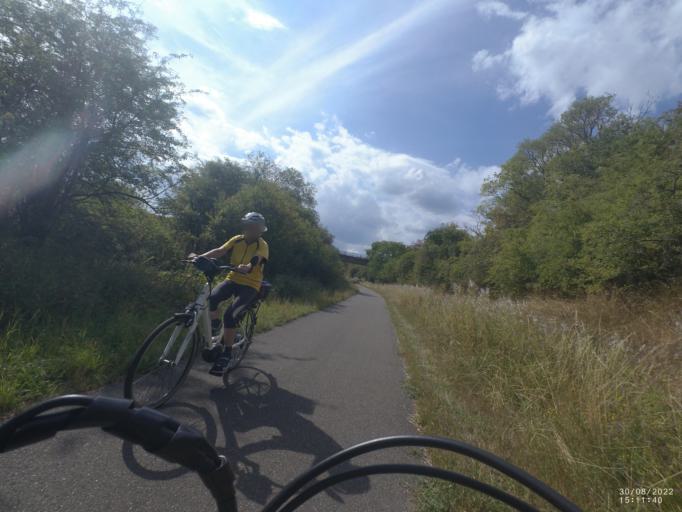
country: DE
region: Rheinland-Pfalz
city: Scheid
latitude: 50.3536
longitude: 6.4118
